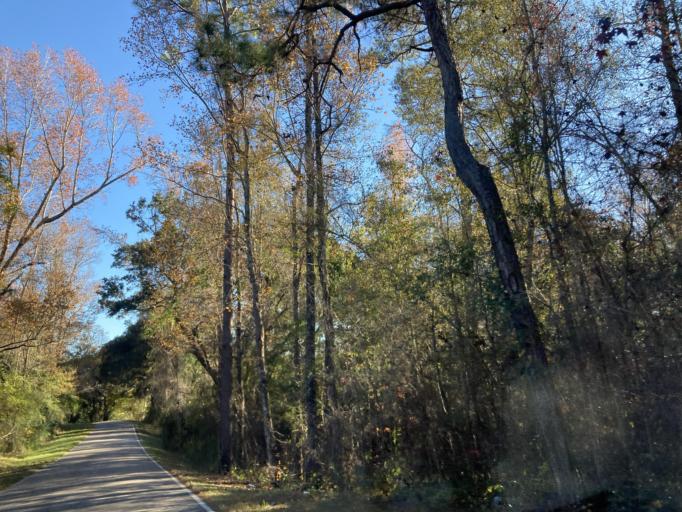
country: US
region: Mississippi
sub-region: Lamar County
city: Sumrall
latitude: 31.3690
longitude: -89.5791
